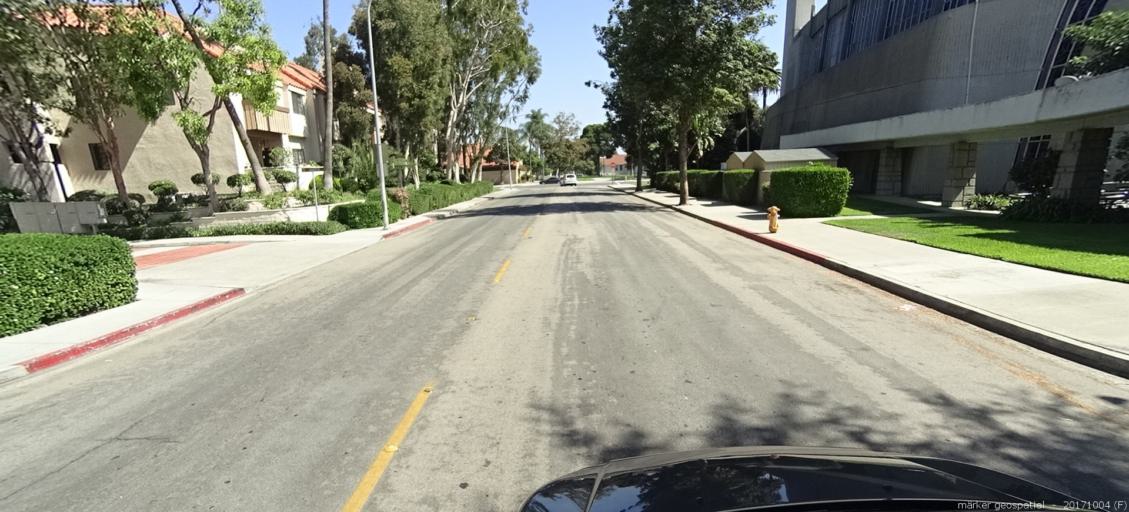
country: US
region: California
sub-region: Orange County
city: Garden Grove
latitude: 33.7778
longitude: -117.9420
